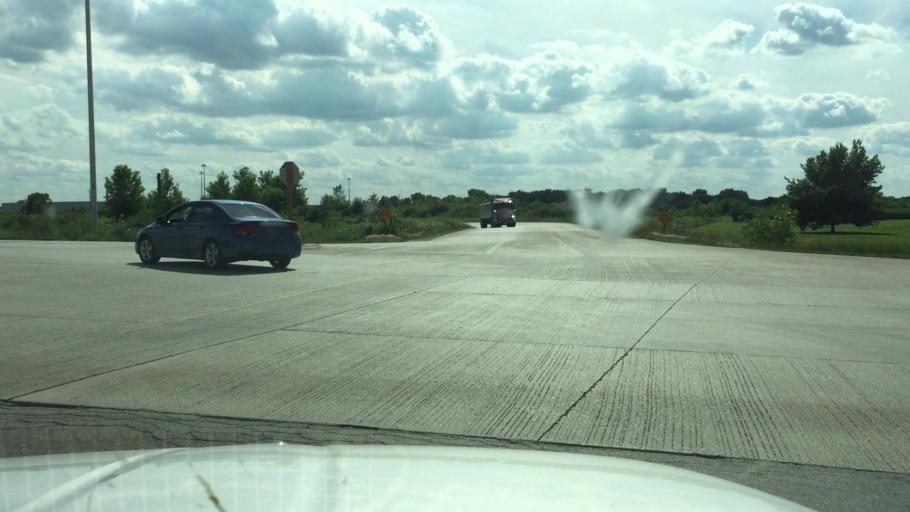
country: US
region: Illinois
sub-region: LaSalle County
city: Deer Park
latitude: 41.3708
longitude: -89.0100
